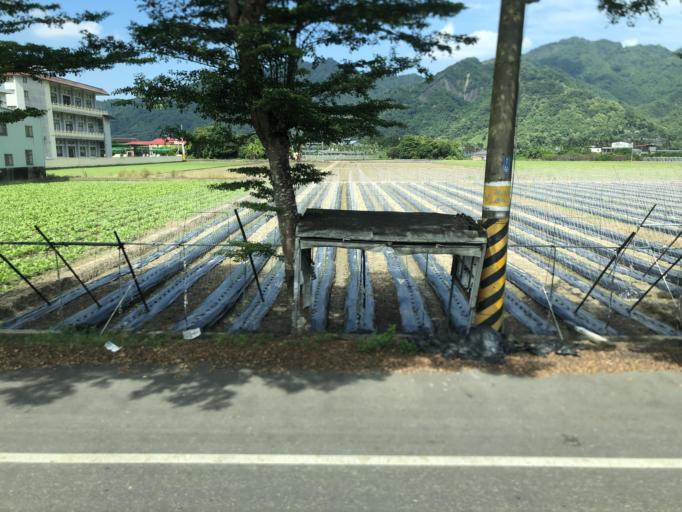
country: TW
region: Taiwan
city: Yujing
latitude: 22.9090
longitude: 120.5604
